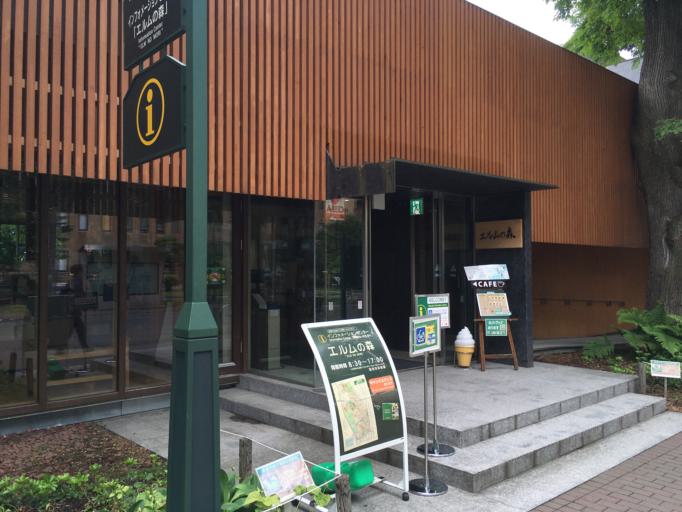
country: JP
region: Hokkaido
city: Sapporo
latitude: 43.0710
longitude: 141.3478
